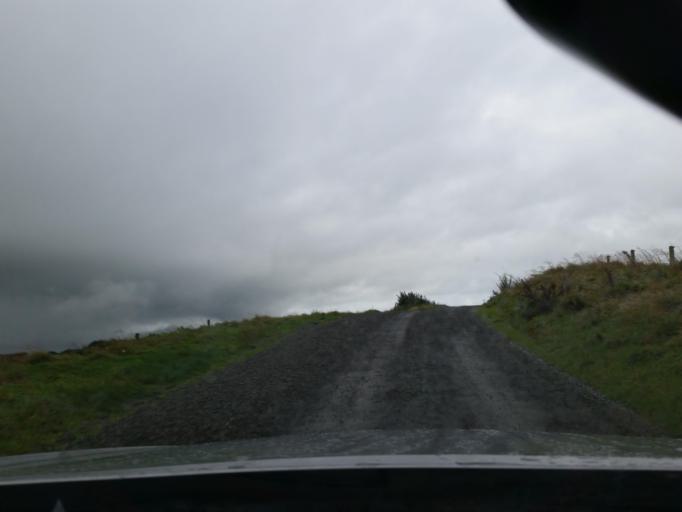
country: NZ
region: Southland
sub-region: Southland District
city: Riverton
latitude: -46.2678
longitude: 168.1436
